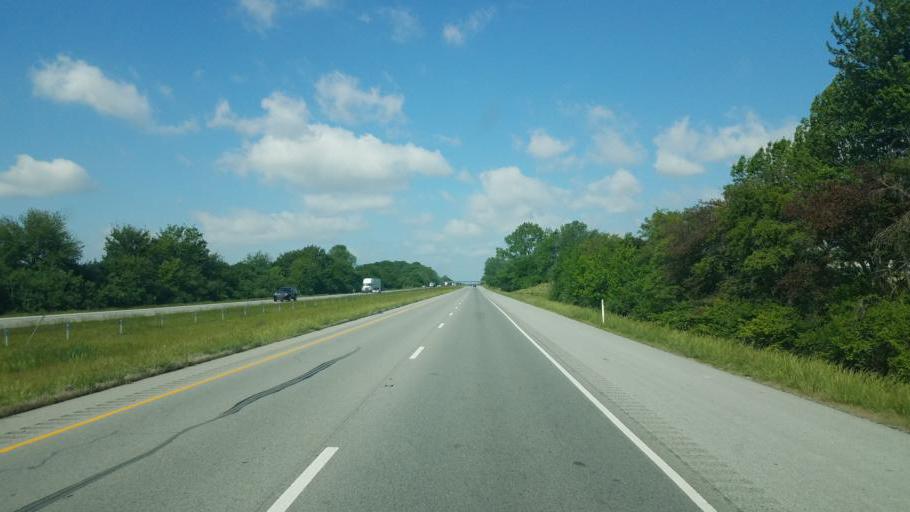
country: US
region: Indiana
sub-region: Putnam County
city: Cloverdale
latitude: 39.5606
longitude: -86.6568
